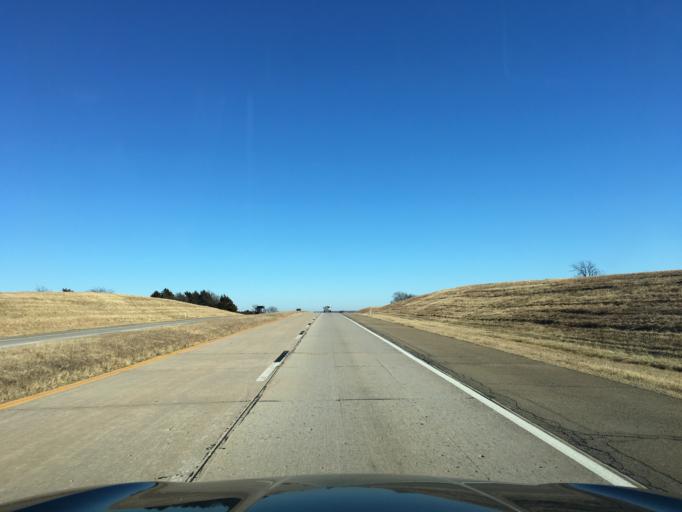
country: US
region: Oklahoma
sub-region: Payne County
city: Yale
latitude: 36.2240
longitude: -96.7342
